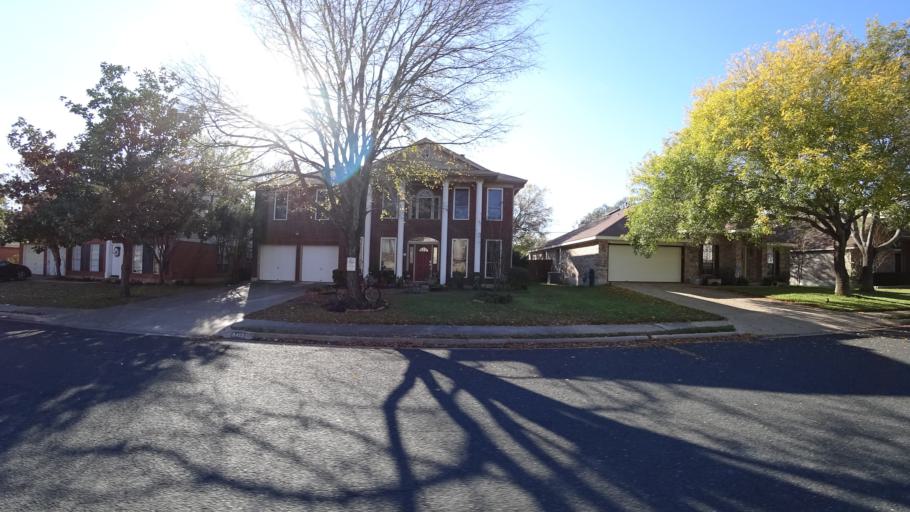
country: US
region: Texas
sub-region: Williamson County
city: Brushy Creek
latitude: 30.4882
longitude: -97.7439
